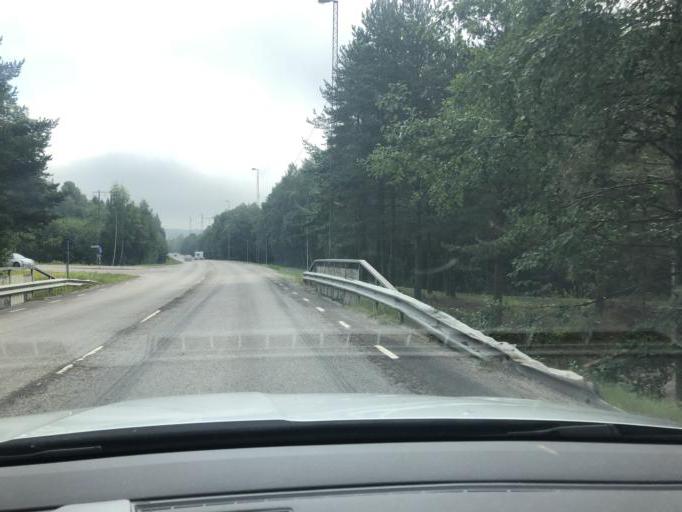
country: SE
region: Vaesternorrland
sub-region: Sundsvalls Kommun
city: Sundsvall
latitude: 62.4115
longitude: 17.3192
